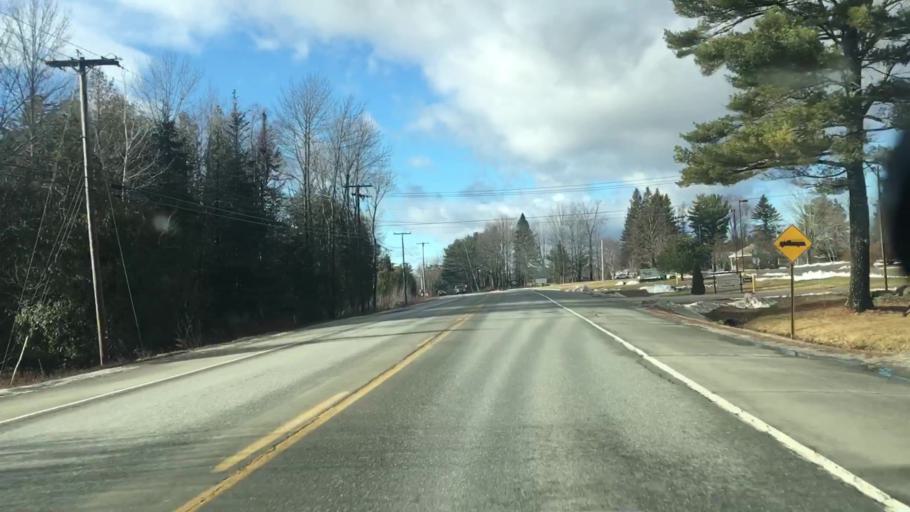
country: US
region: Maine
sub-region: Penobscot County
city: Holden
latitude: 44.7545
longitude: -68.6604
